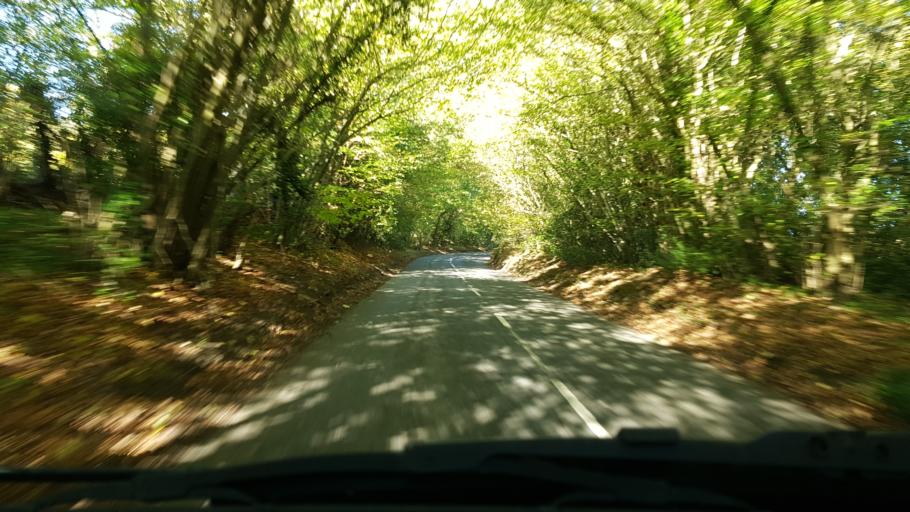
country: GB
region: England
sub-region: Surrey
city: Ockley
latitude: 51.1746
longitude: -0.4077
